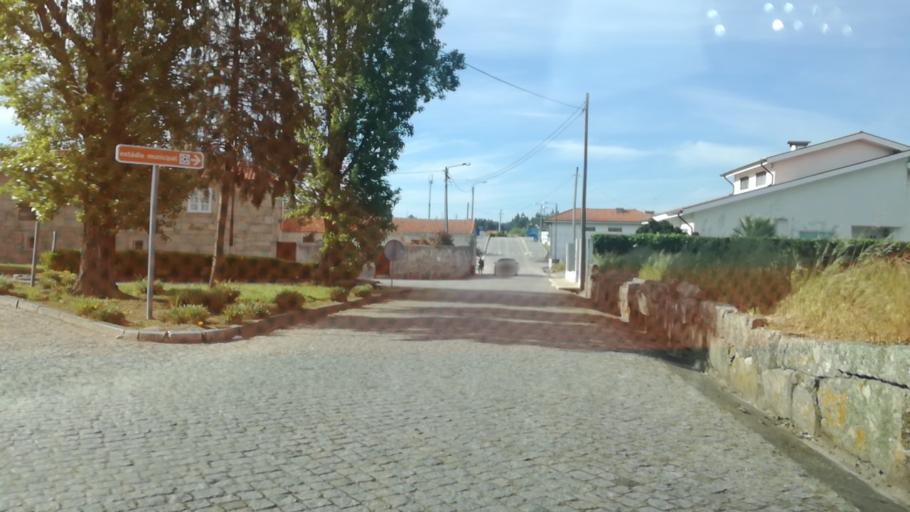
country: PT
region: Porto
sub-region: Maia
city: Nogueira
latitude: 41.2361
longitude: -8.5920
